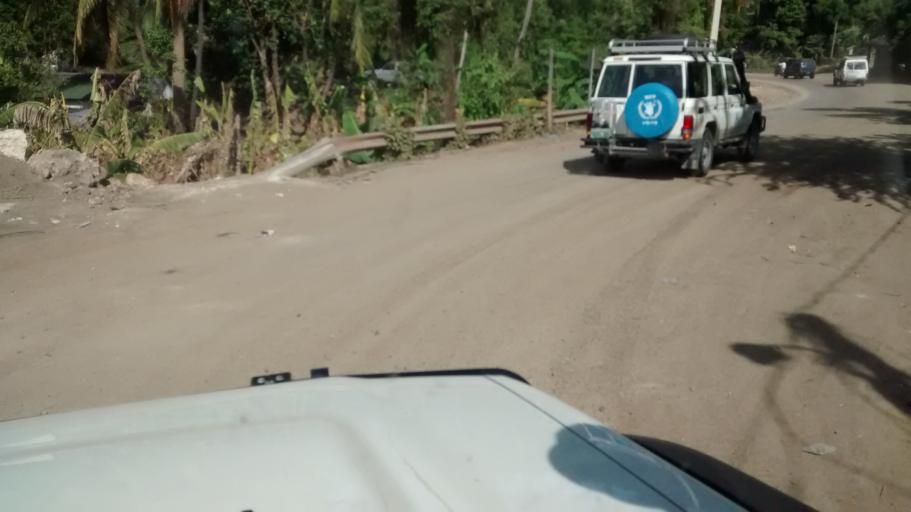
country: HT
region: Ouest
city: Tigwav
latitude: 18.4364
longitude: -72.8447
